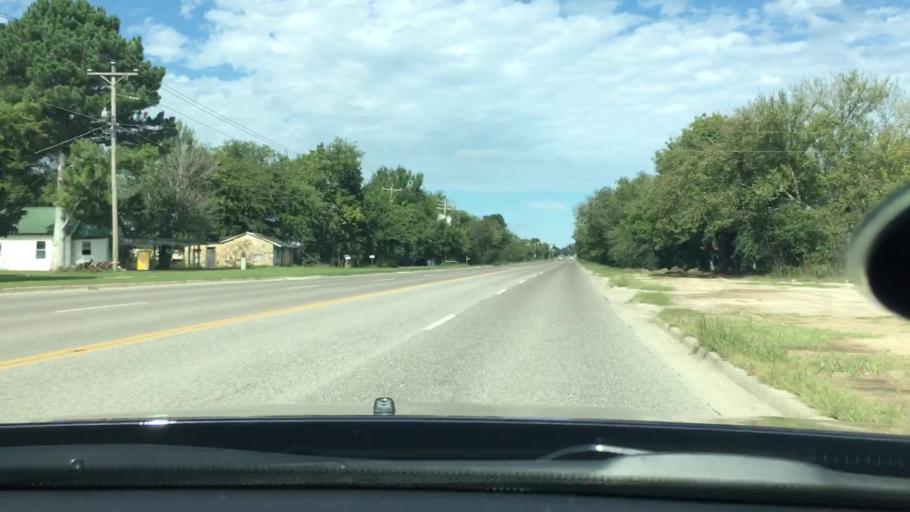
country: US
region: Oklahoma
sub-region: Murray County
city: Davis
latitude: 34.4871
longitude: -97.1300
